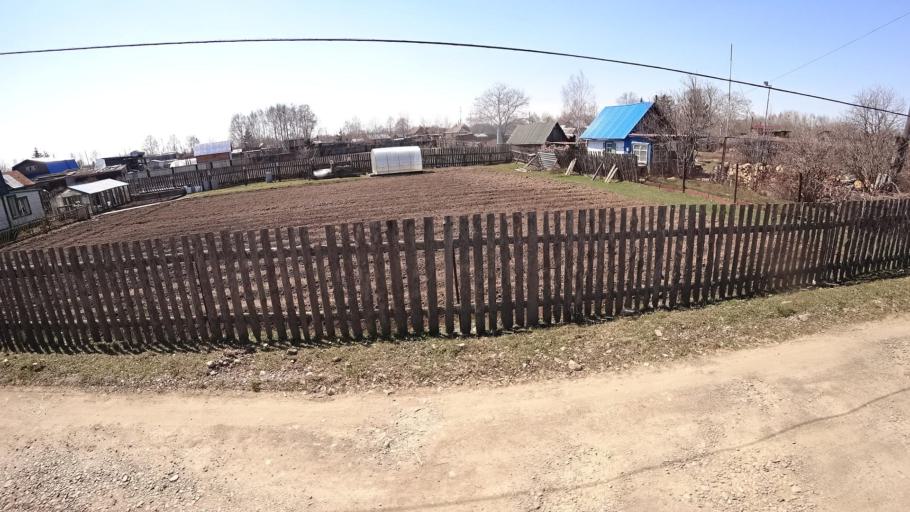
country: RU
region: Khabarovsk Krai
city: Khurba
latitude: 50.4120
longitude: 136.8881
